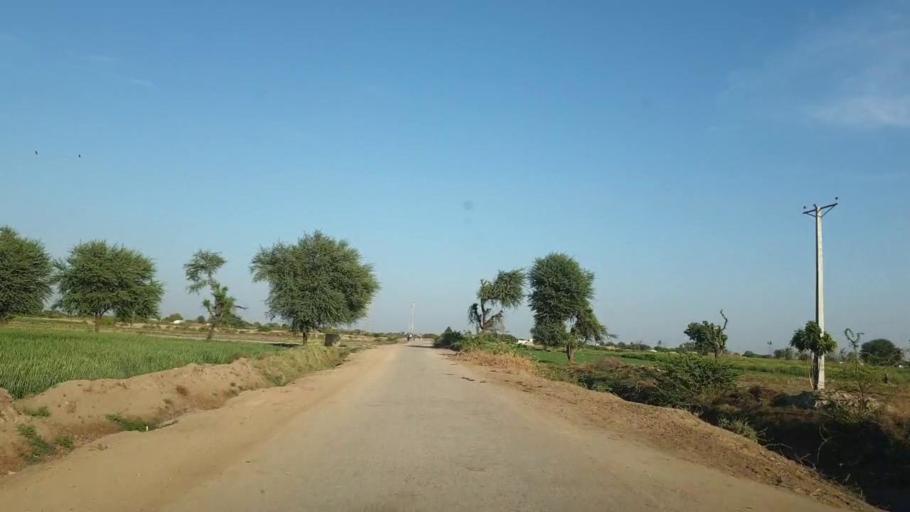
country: PK
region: Sindh
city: Kunri
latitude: 25.0911
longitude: 69.4266
